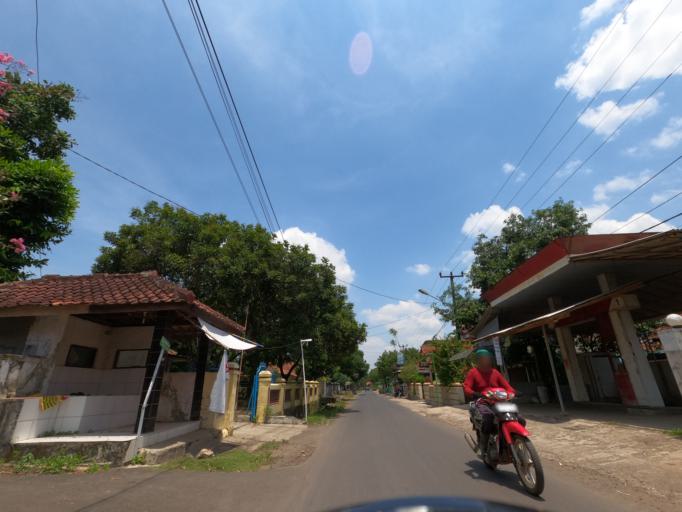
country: ID
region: West Java
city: Pamanukan
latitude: -6.5346
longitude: 107.7709
